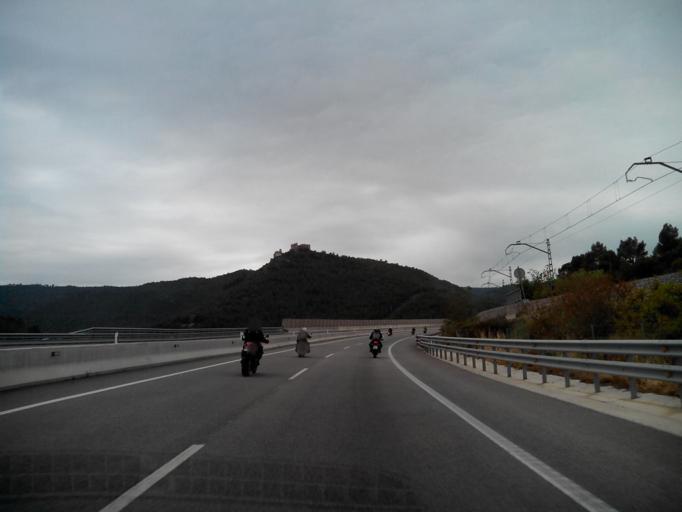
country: ES
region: Catalonia
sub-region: Provincia de Barcelona
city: Fonollosa
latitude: 41.7314
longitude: 1.6605
